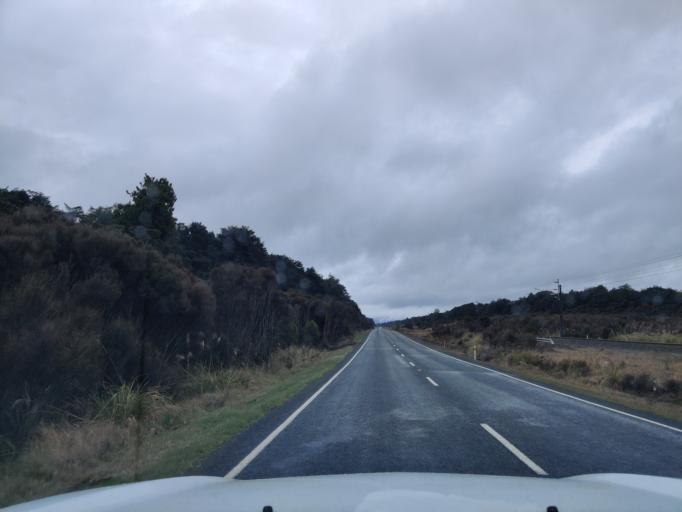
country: NZ
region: Manawatu-Wanganui
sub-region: Ruapehu District
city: Waiouru
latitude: -39.3212
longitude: 175.3857
